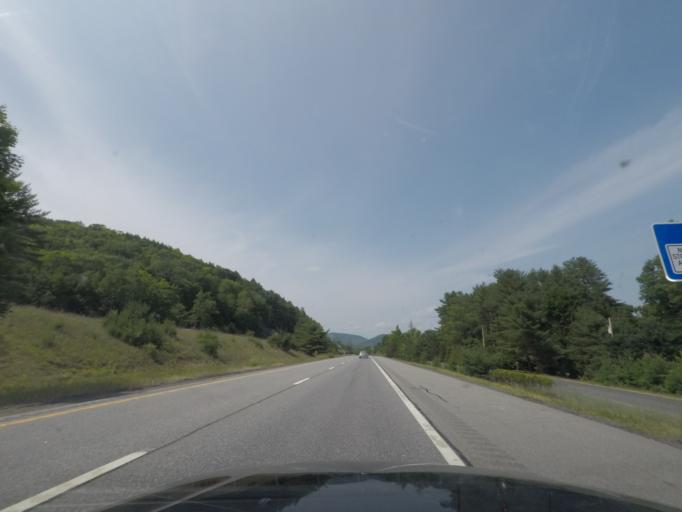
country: US
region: New York
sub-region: Warren County
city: Warrensburg
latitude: 43.7100
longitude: -73.8095
